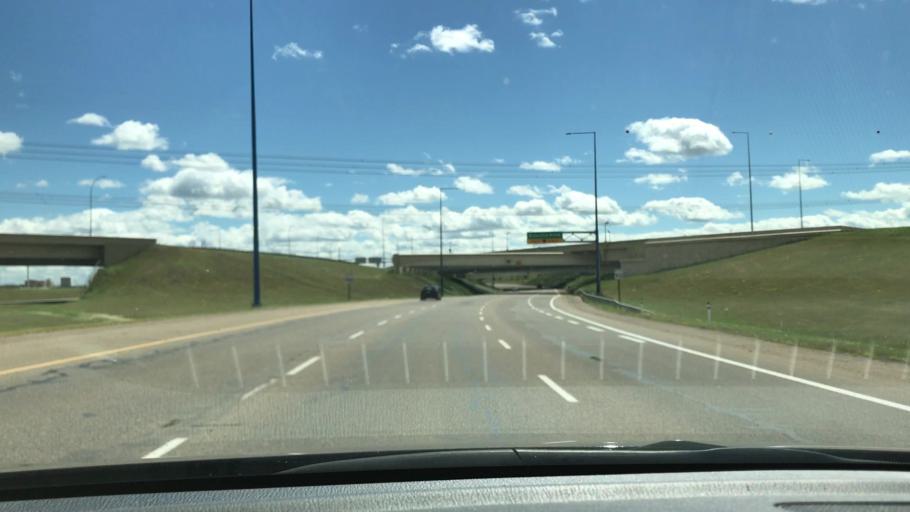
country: CA
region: Alberta
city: Beaumont
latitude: 53.4347
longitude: -113.4908
